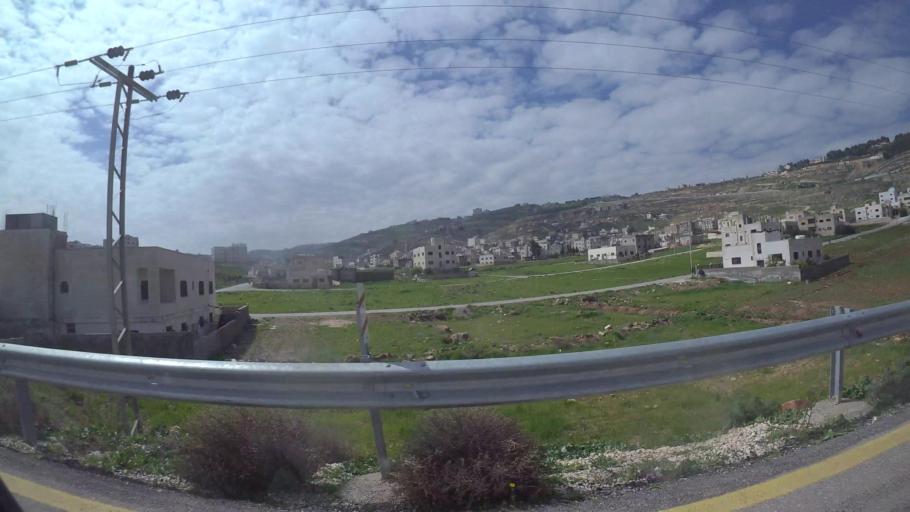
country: JO
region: Amman
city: Al Jubayhah
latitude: 32.0612
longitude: 35.8109
